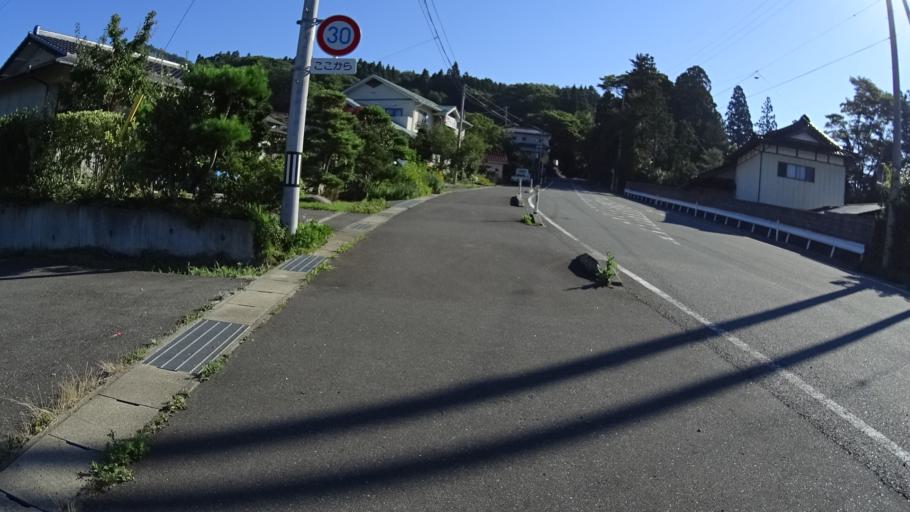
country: JP
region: Iwate
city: Ofunato
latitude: 38.8644
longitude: 141.6189
